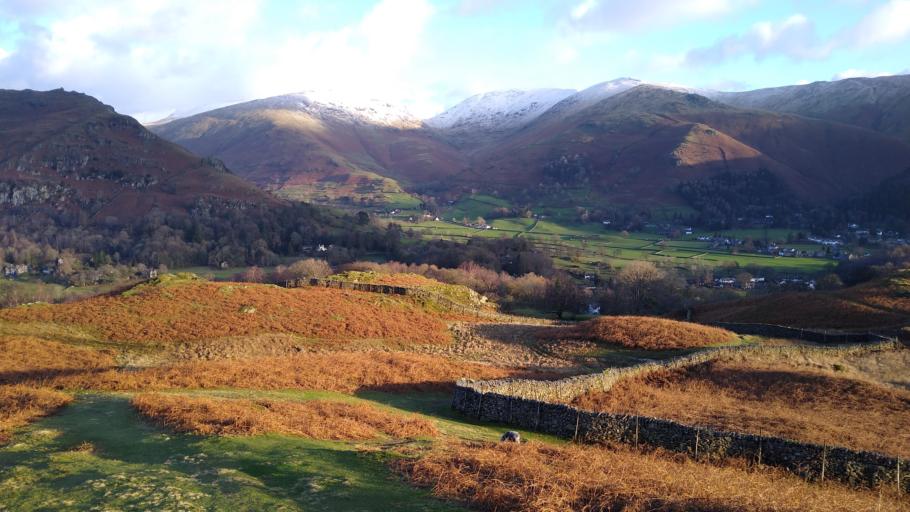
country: GB
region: England
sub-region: Cumbria
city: Ambleside
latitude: 54.4584
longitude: -3.0401
